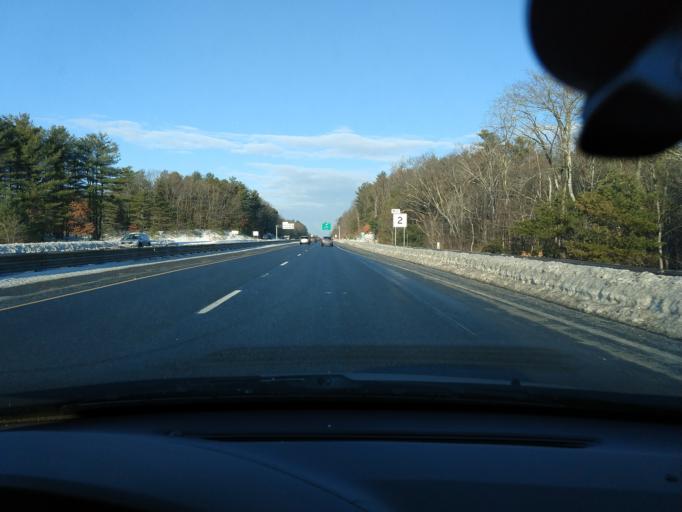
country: US
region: Massachusetts
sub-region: Middlesex County
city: Littleton Common
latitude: 42.5009
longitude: -71.4759
